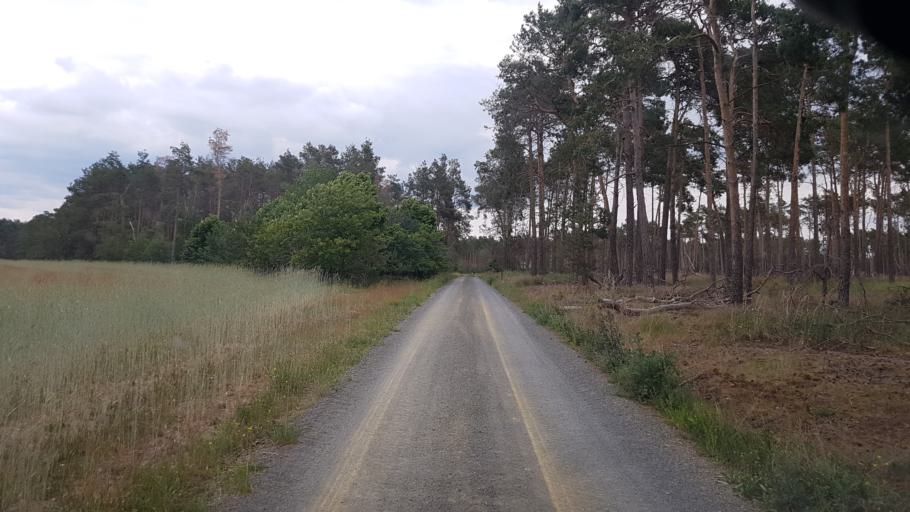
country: DE
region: Brandenburg
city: Schlieben
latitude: 51.6809
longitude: 13.3598
